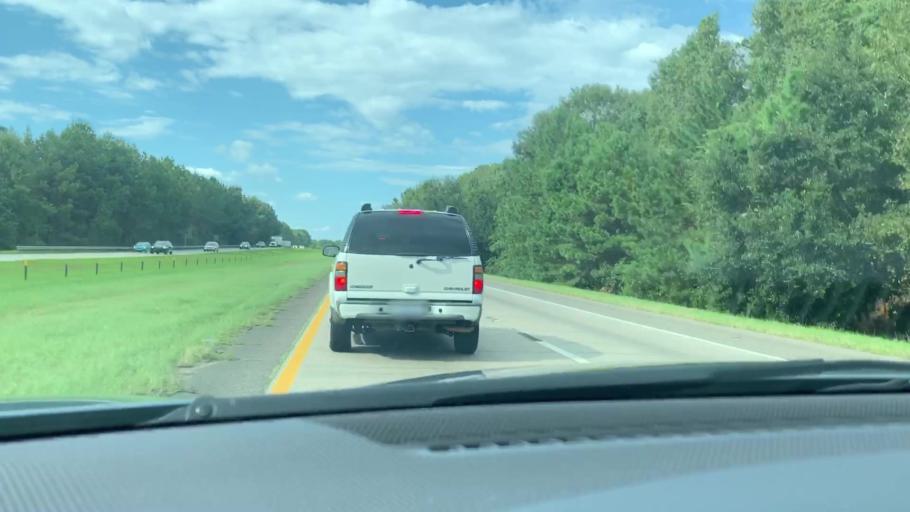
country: US
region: South Carolina
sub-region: Hampton County
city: Yemassee
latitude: 32.6397
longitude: -80.8828
